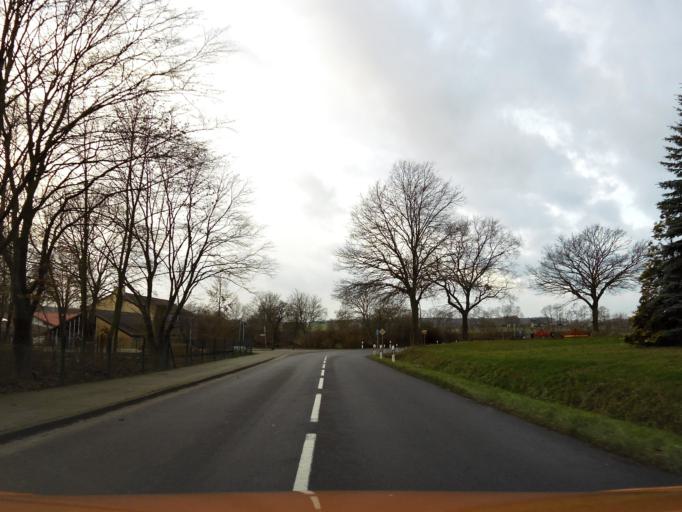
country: DE
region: Lower Saxony
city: Gross Twulpstedt
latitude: 52.3755
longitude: 10.9163
